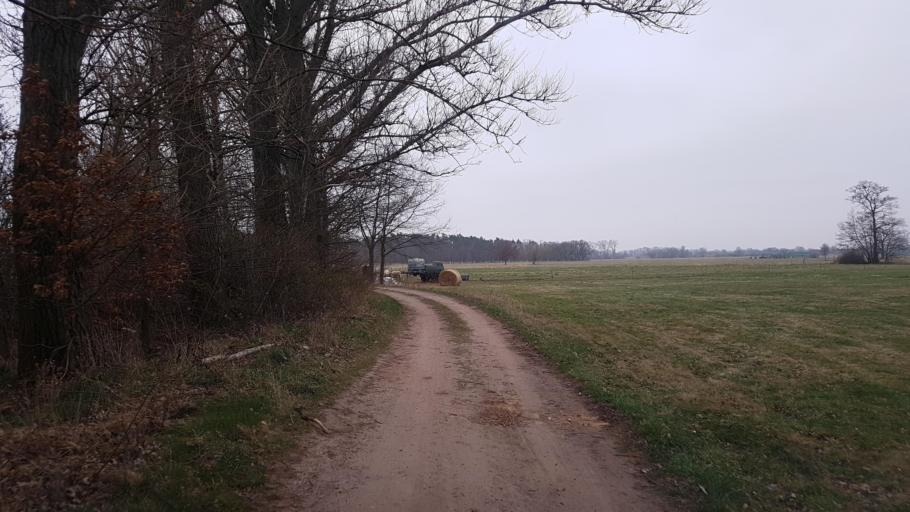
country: DE
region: Saxony
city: Nauwalde
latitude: 51.4376
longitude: 13.3760
